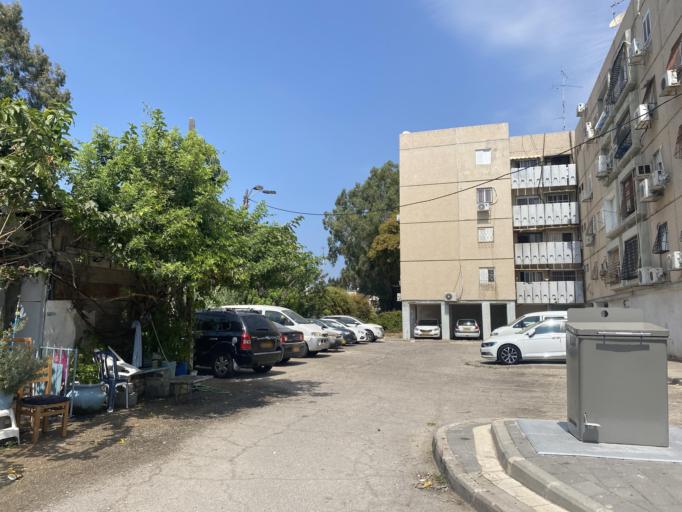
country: IL
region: Tel Aviv
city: Azor
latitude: 32.0450
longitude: 34.7997
